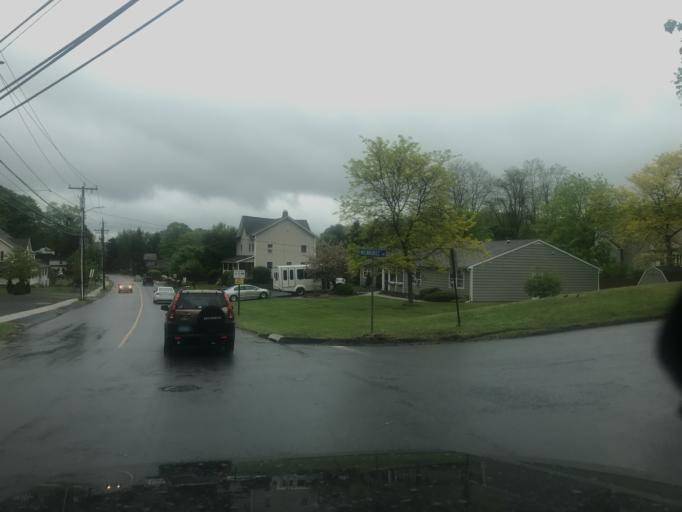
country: US
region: Connecticut
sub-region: Fairfield County
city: Bethel
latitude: 41.3745
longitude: -73.4065
